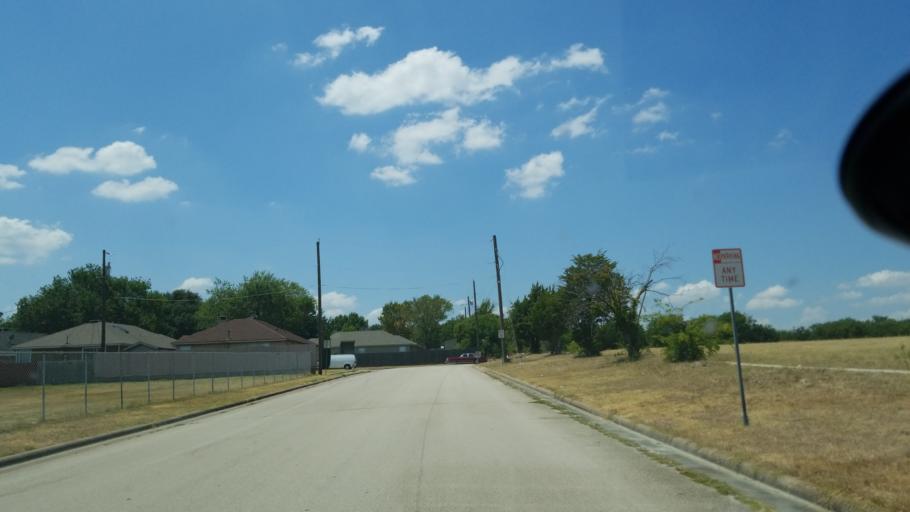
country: US
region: Texas
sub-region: Dallas County
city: Duncanville
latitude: 32.6660
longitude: -96.8922
